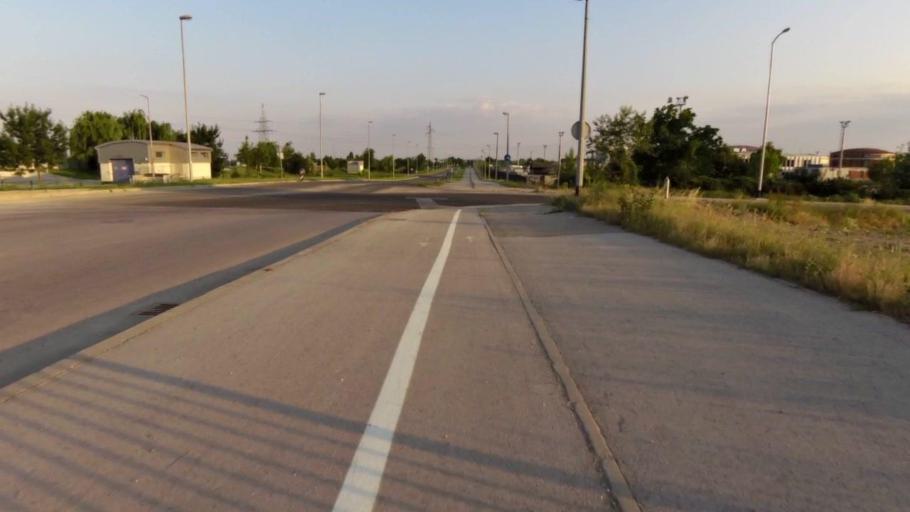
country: HR
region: Grad Zagreb
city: Dubrava
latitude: 45.7933
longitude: 16.0790
